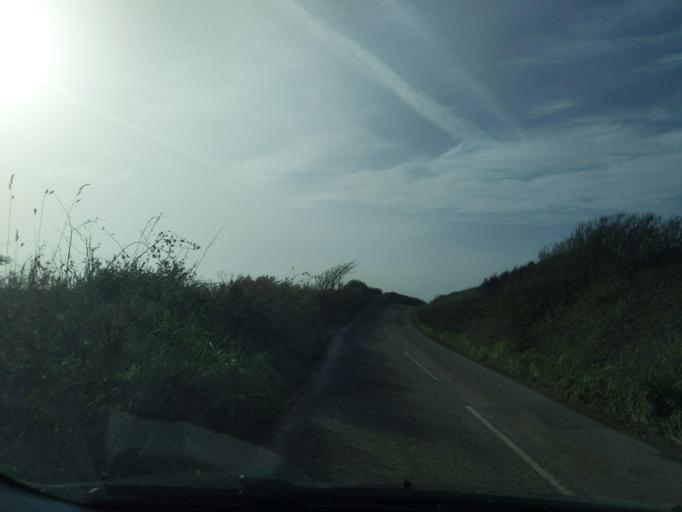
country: GB
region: England
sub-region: Cornwall
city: Pillaton
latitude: 50.3641
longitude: -4.3186
